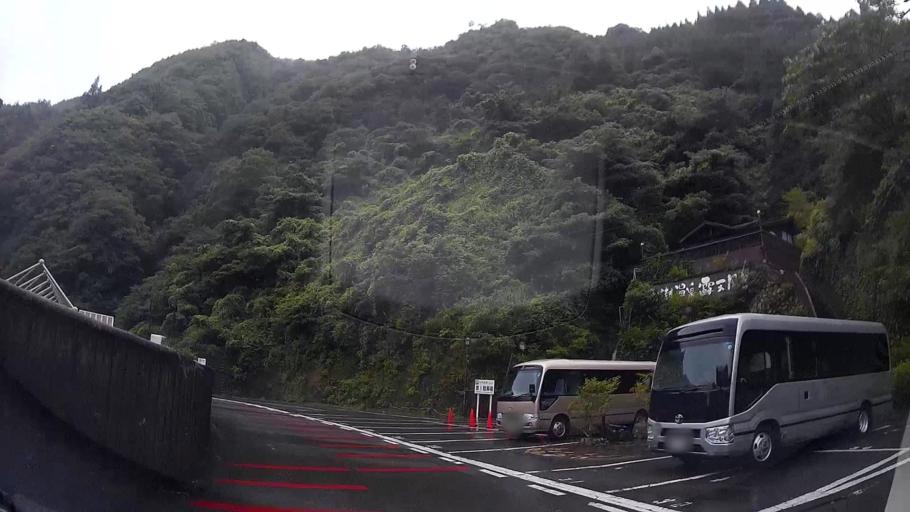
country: JP
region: Oita
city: Tsukawaki
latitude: 33.1870
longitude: 131.0305
